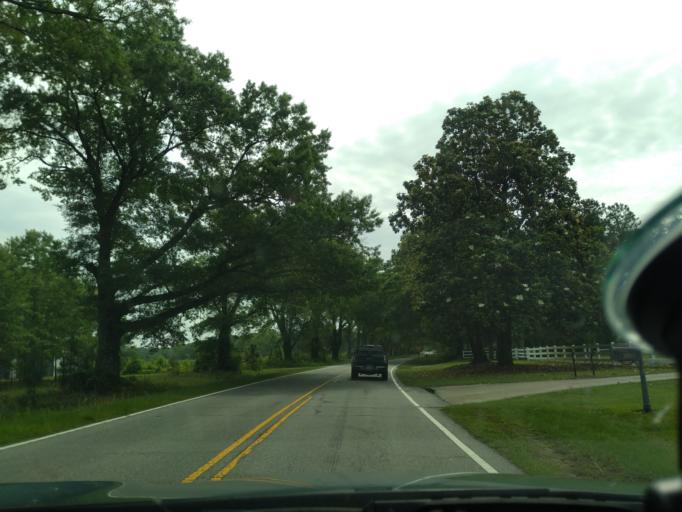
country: US
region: North Carolina
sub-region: Washington County
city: Plymouth
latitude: 35.9043
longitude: -76.6812
